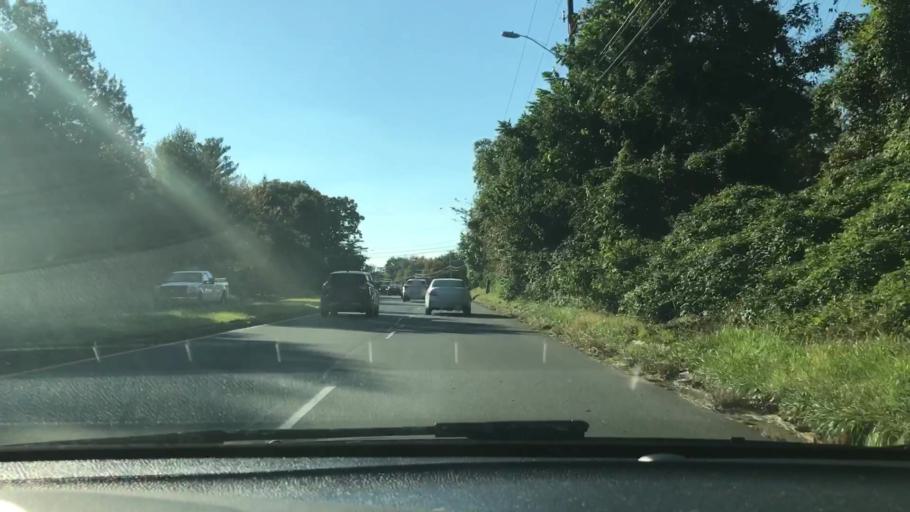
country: US
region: Virginia
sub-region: Fairfax County
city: Annandale
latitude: 38.8359
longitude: -77.1802
